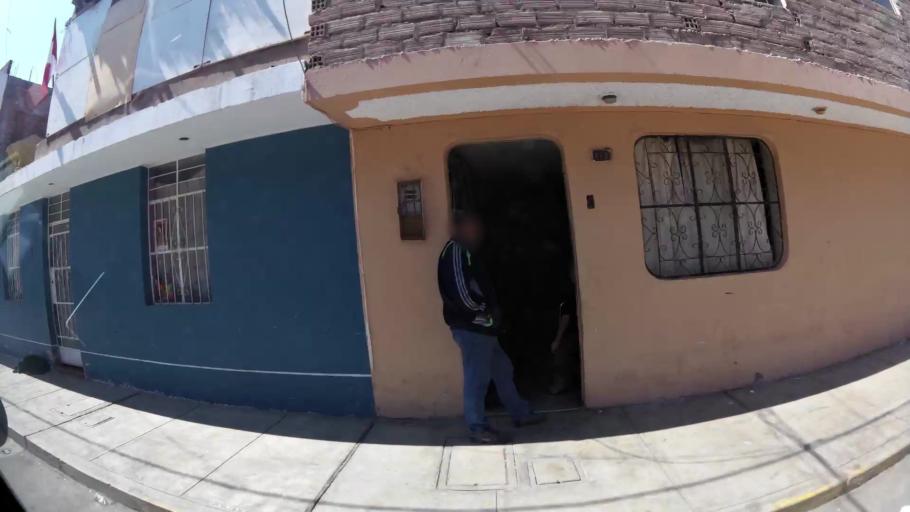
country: PE
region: Ica
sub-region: Provincia de Ica
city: Ica
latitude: -14.0699
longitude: -75.7233
